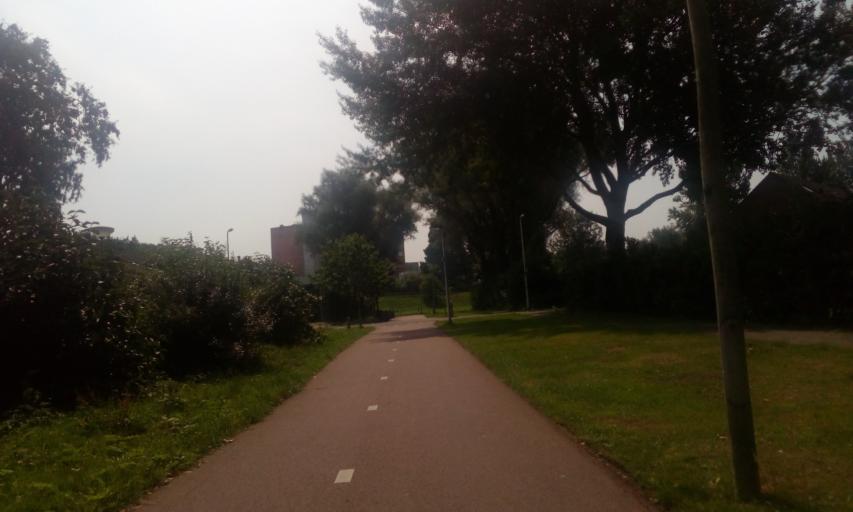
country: NL
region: South Holland
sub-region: Gemeente Capelle aan den IJssel
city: Capelle aan den IJssel
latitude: 51.9563
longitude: 4.5808
